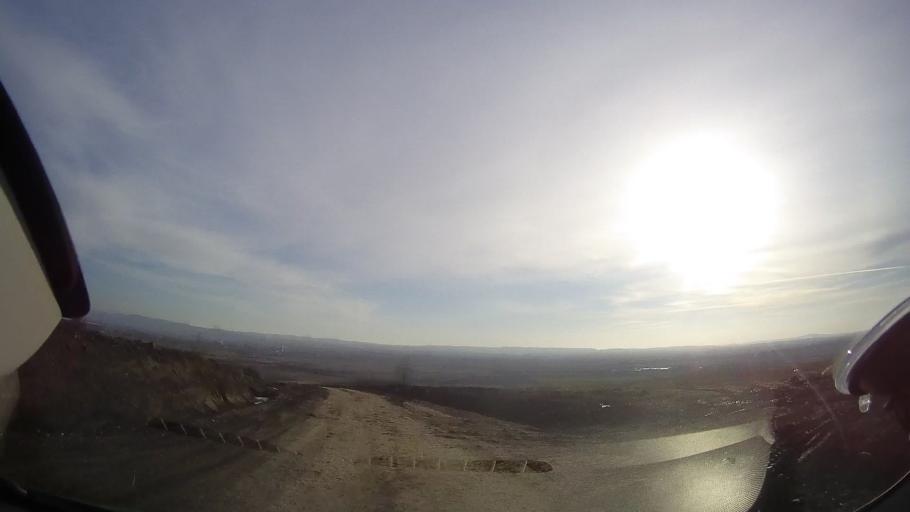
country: RO
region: Bihor
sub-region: Comuna Tileagd
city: Tileagd
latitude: 47.0986
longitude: 22.1765
